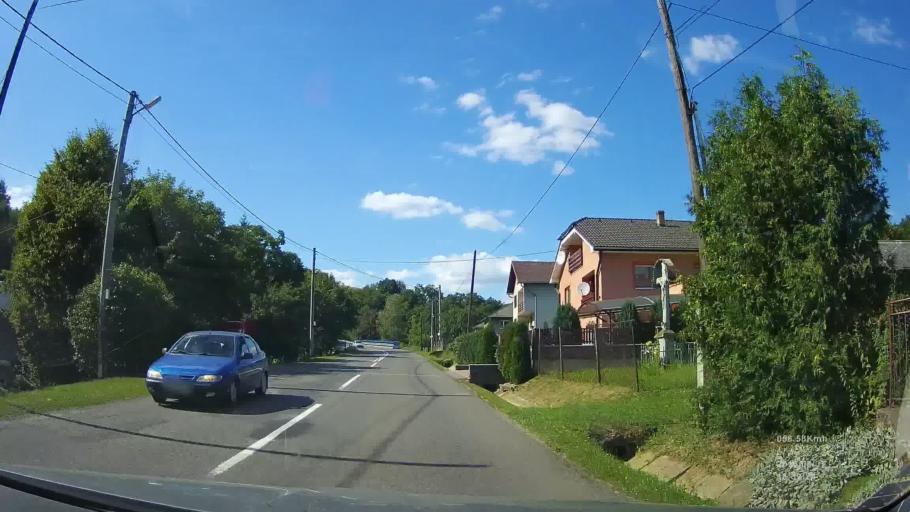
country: SK
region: Presovsky
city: Giraltovce
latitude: 49.1179
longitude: 21.6040
